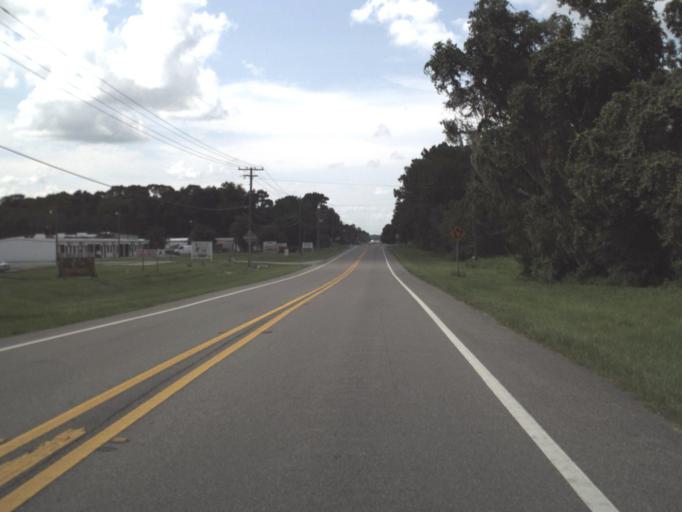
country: US
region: Florida
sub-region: Citrus County
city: Floral City
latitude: 28.7858
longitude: -82.2996
